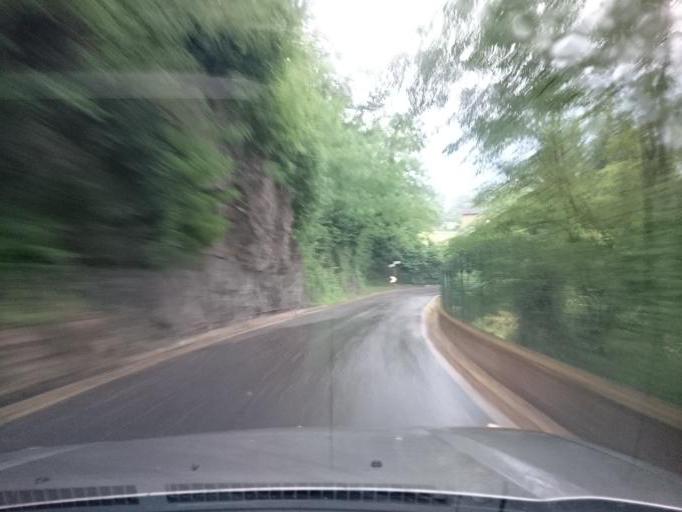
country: IT
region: Lombardy
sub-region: Provincia di Brescia
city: Capo di Ponte
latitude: 46.0382
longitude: 10.3533
